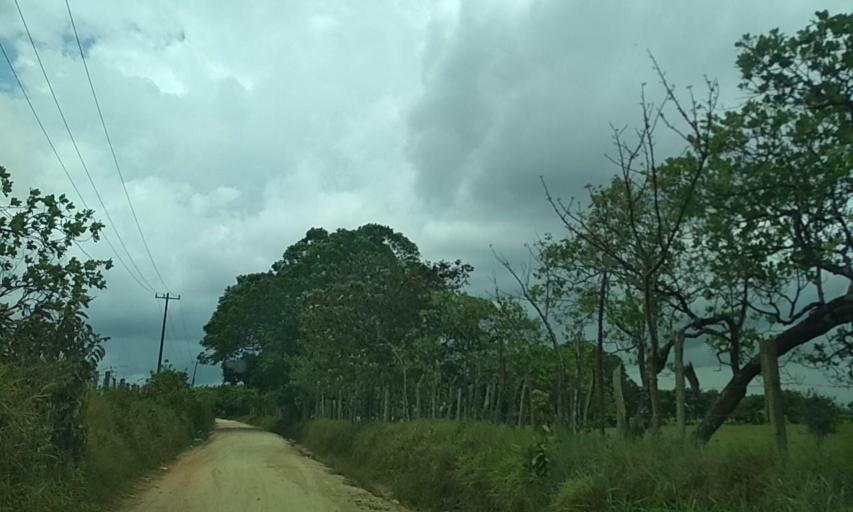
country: MX
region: Veracruz
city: Las Choapas
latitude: 17.8918
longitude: -94.1174
